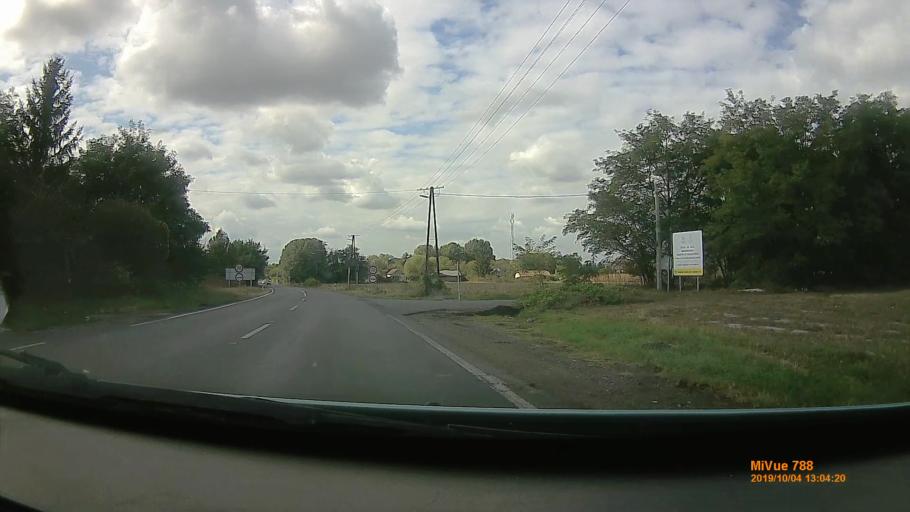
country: HU
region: Szabolcs-Szatmar-Bereg
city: Nyirtelek
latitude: 47.9588
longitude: 21.6291
